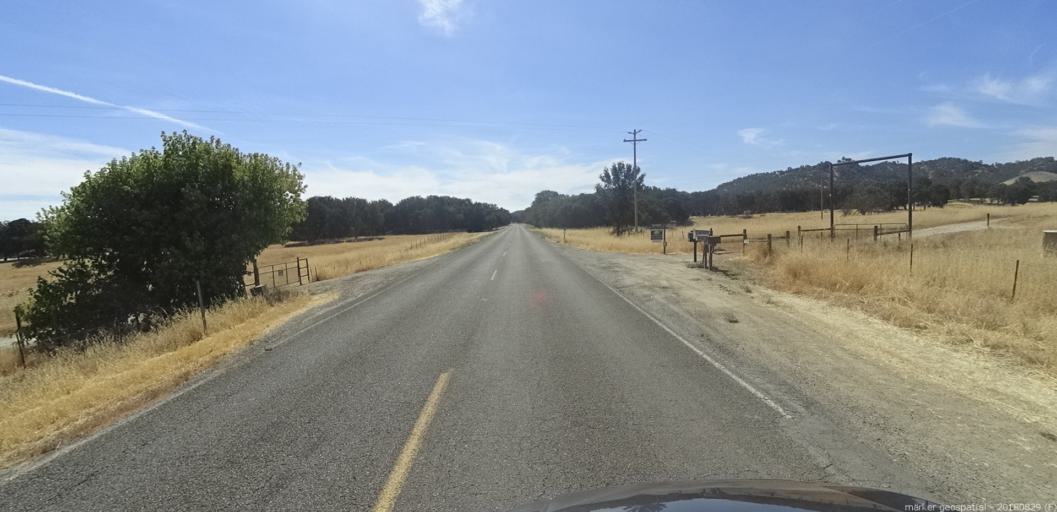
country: US
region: California
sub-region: San Luis Obispo County
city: Lake Nacimiento
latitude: 35.8328
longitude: -121.0262
